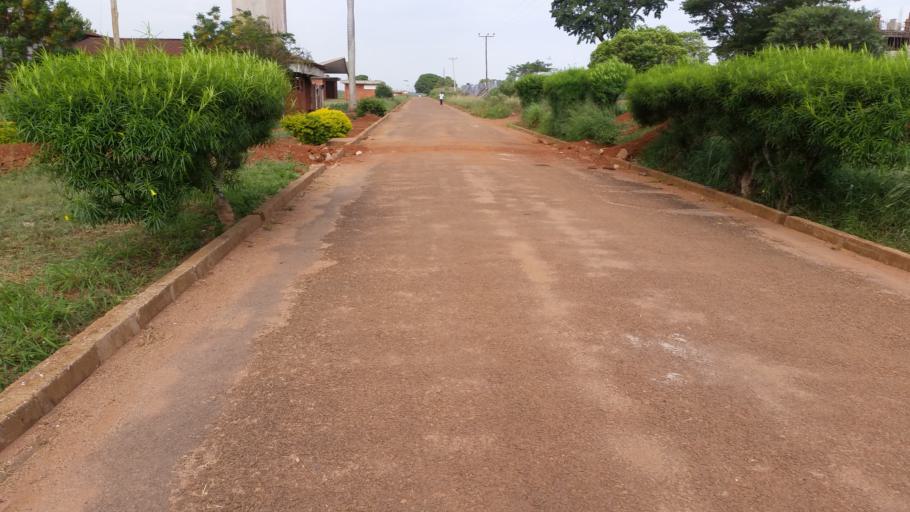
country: UG
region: Eastern Region
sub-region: Busia District
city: Busia
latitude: 0.5459
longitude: 34.0215
